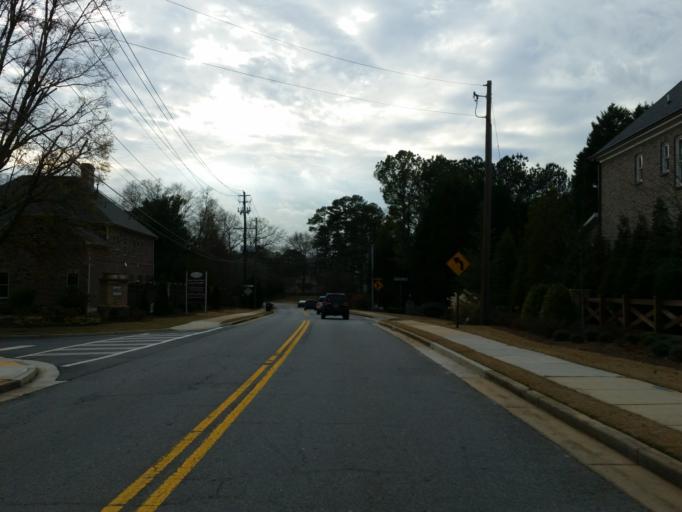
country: US
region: Georgia
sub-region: Fulton County
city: Sandy Springs
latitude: 33.9766
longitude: -84.4431
